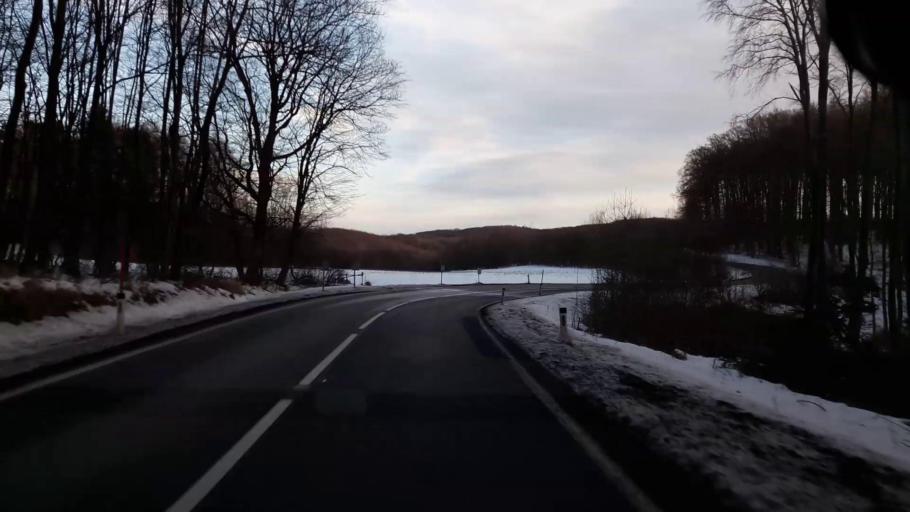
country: AT
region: Lower Austria
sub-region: Politischer Bezirk Wien-Umgebung
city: Mauerbach
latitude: 48.2742
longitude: 16.1872
